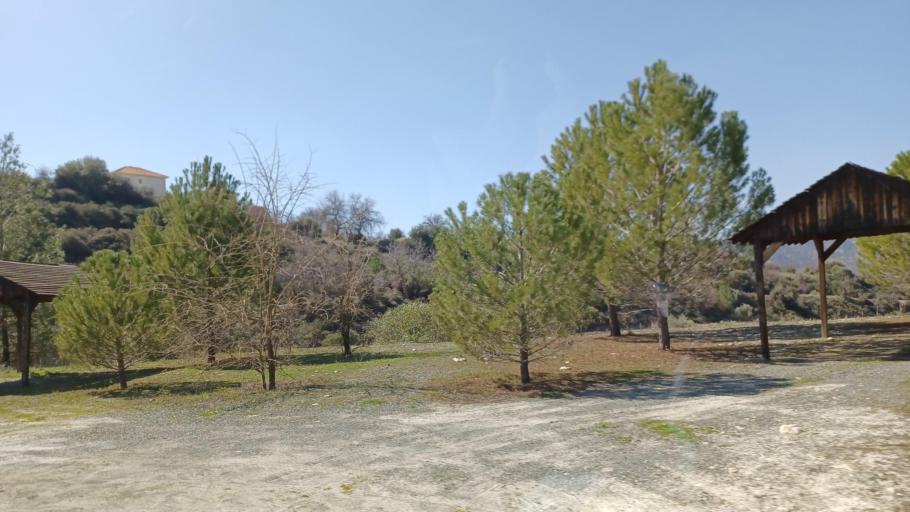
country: CY
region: Limassol
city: Pelendri
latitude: 34.8299
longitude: 32.9220
